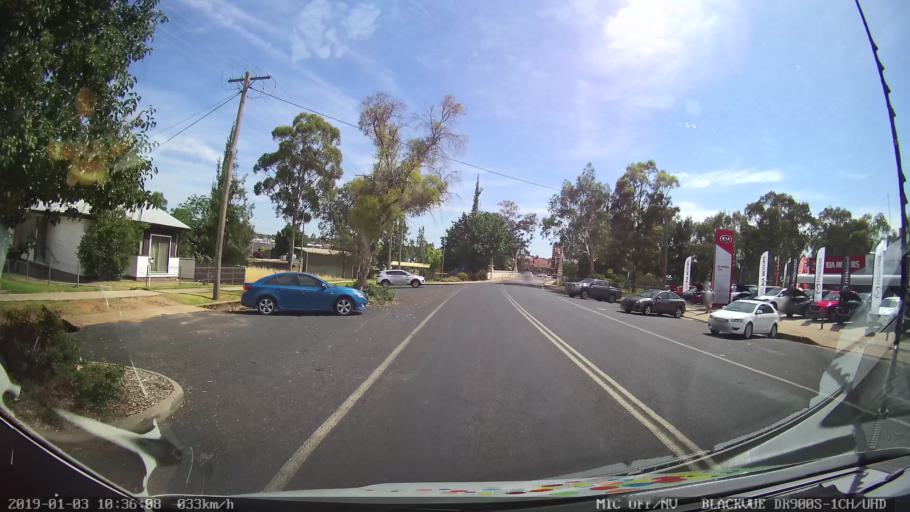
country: AU
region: New South Wales
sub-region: Young
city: Young
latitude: -34.3167
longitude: 148.2967
